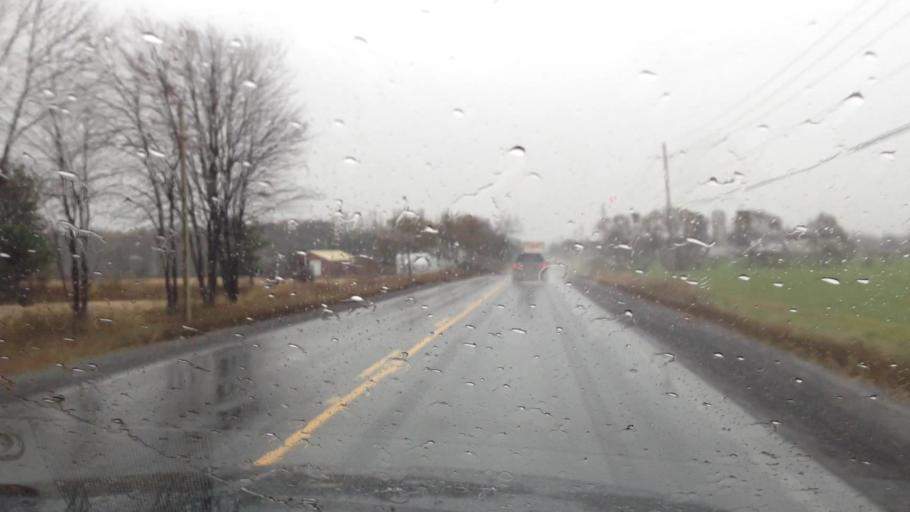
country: CA
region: Ontario
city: Bourget
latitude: 45.2800
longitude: -75.3166
